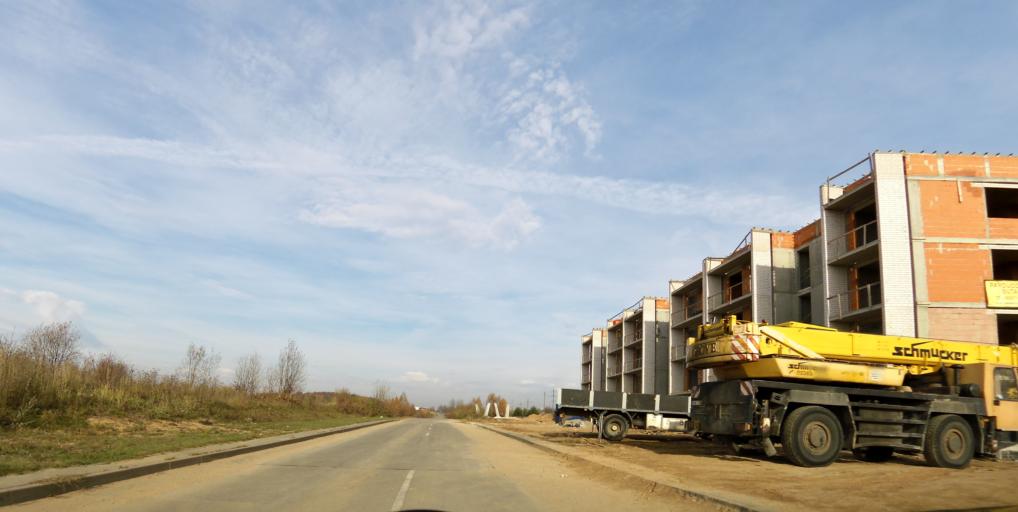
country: LT
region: Vilnius County
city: Justiniskes
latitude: 54.7065
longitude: 25.2061
